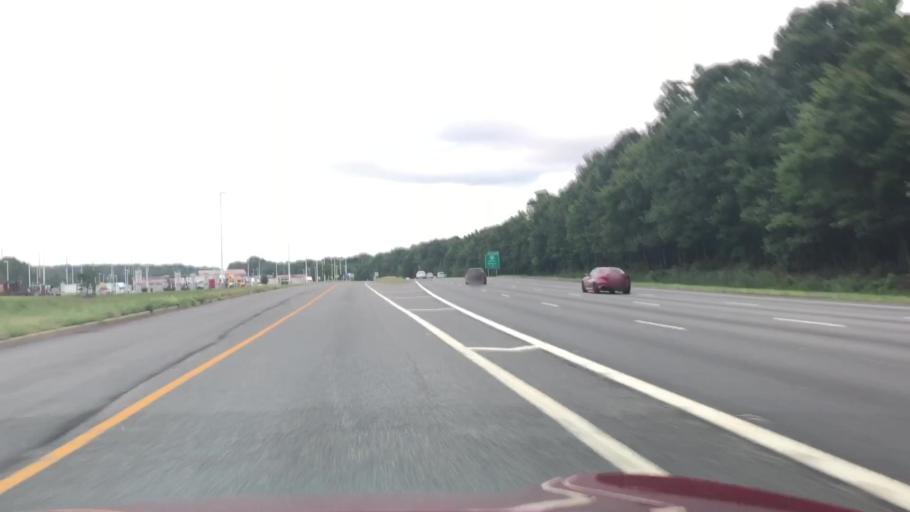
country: US
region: Delaware
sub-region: New Castle County
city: Brookside
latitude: 39.6584
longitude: -75.6957
